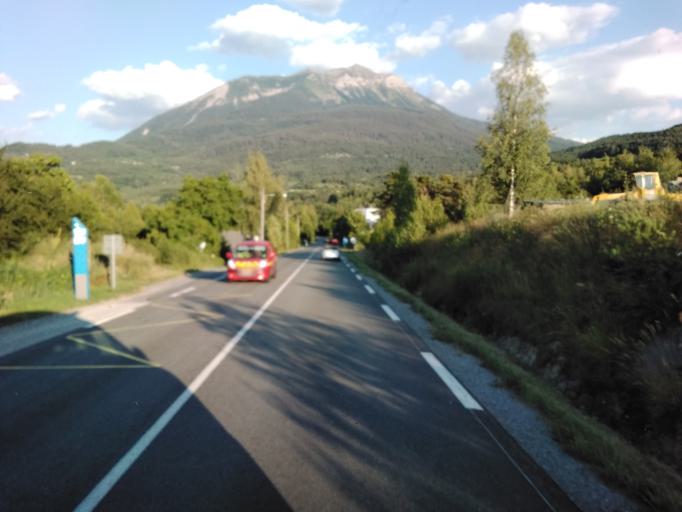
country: FR
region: Provence-Alpes-Cote d'Azur
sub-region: Departement des Alpes-de-Haute-Provence
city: Seyne-les-Alpes
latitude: 44.4468
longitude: 6.3387
